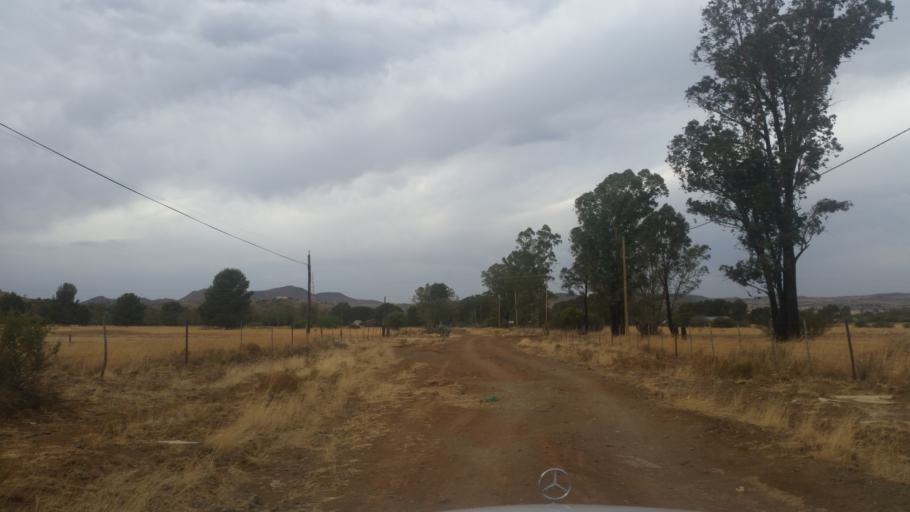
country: ZA
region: Orange Free State
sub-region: Xhariep District Municipality
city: Trompsburg
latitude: -30.4986
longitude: 25.9616
